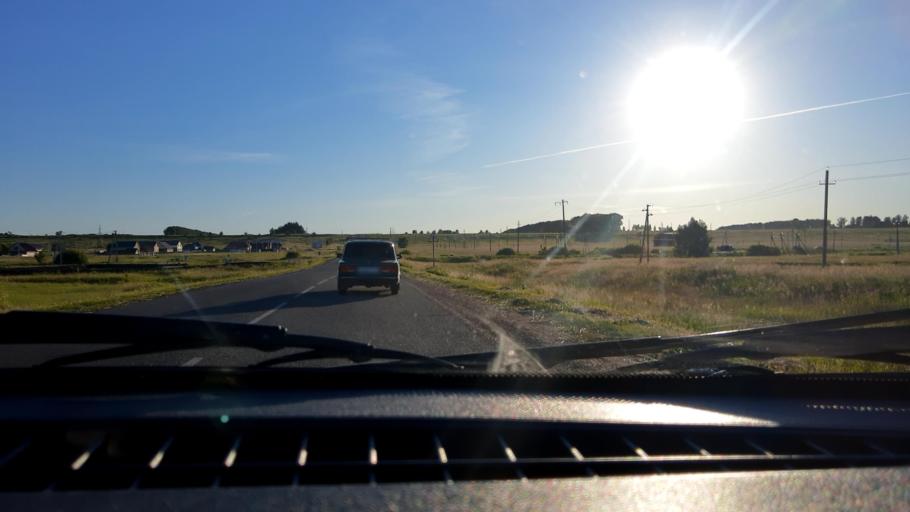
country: RU
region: Bashkortostan
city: Mikhaylovka
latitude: 54.8884
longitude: 55.8830
